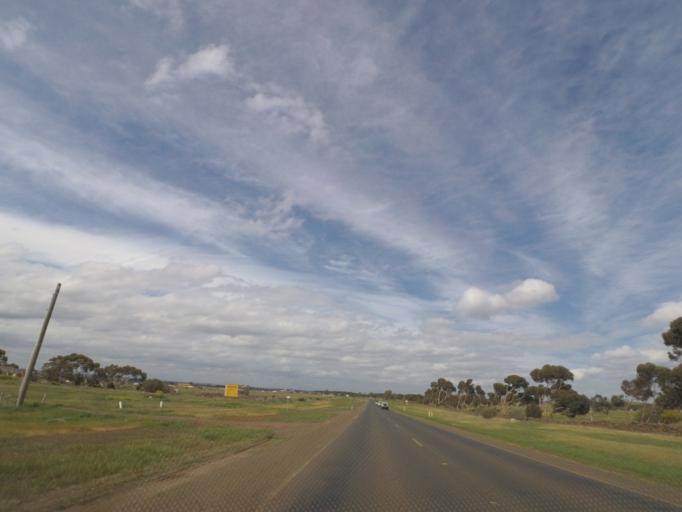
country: AU
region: Victoria
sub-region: Melton
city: Rockbank
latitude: -37.7446
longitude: 144.6563
